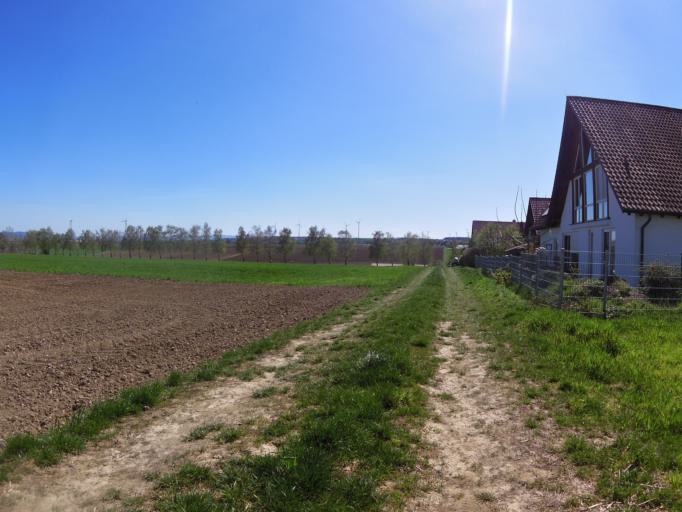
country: DE
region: Bavaria
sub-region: Regierungsbezirk Unterfranken
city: Biebelried
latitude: 49.7986
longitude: 10.0895
